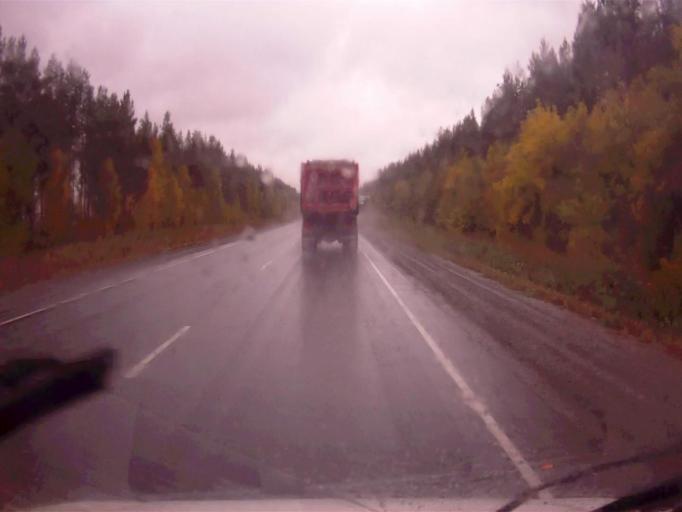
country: RU
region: Chelyabinsk
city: Roshchino
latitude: 55.3588
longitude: 61.2309
